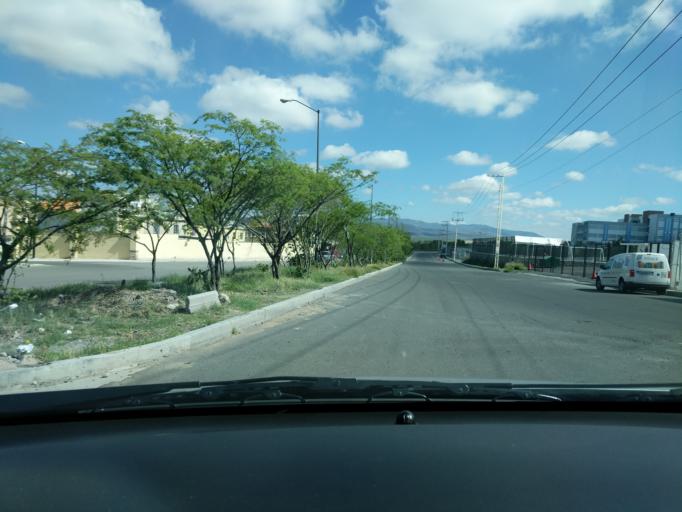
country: MX
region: Queretaro
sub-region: Queretaro
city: Patria Nueva
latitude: 20.6459
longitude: -100.4829
